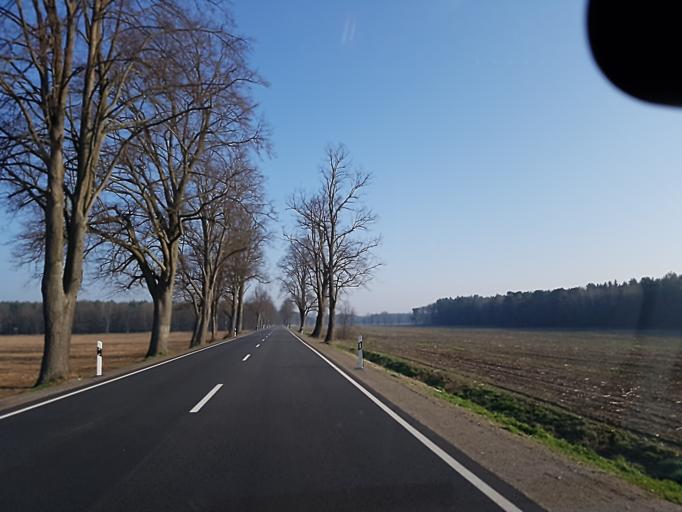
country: DE
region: Brandenburg
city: Bronkow
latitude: 51.6770
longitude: 13.9144
